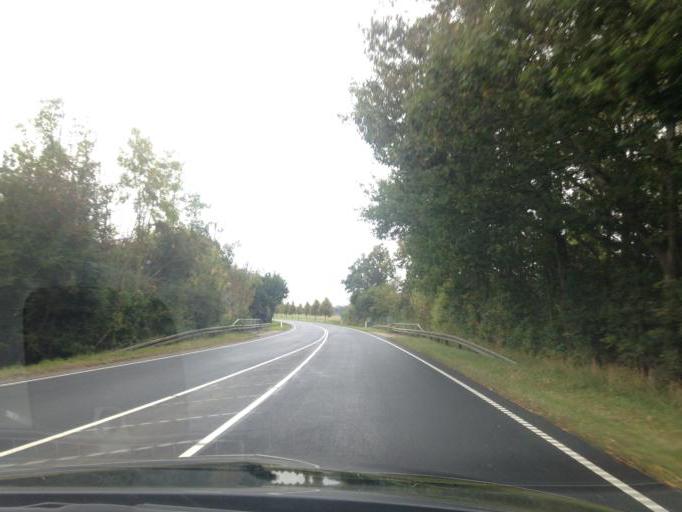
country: DK
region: South Denmark
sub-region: Kolding Kommune
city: Christiansfeld
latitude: 55.3652
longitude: 9.4819
